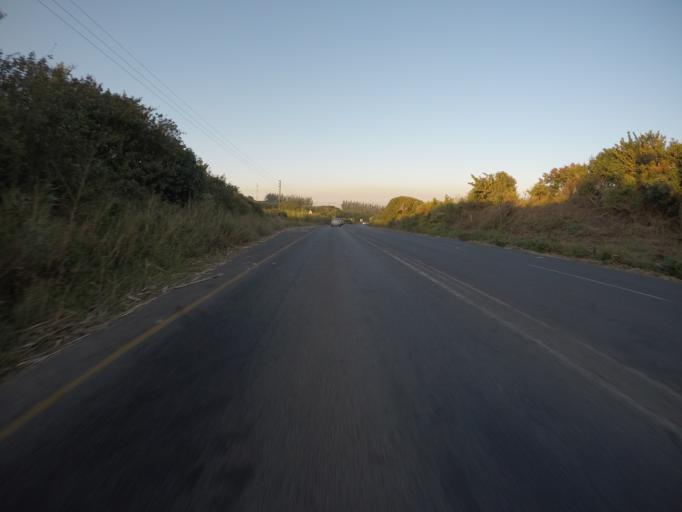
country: ZA
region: KwaZulu-Natal
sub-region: uThungulu District Municipality
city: Empangeni
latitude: -28.8104
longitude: 31.8913
